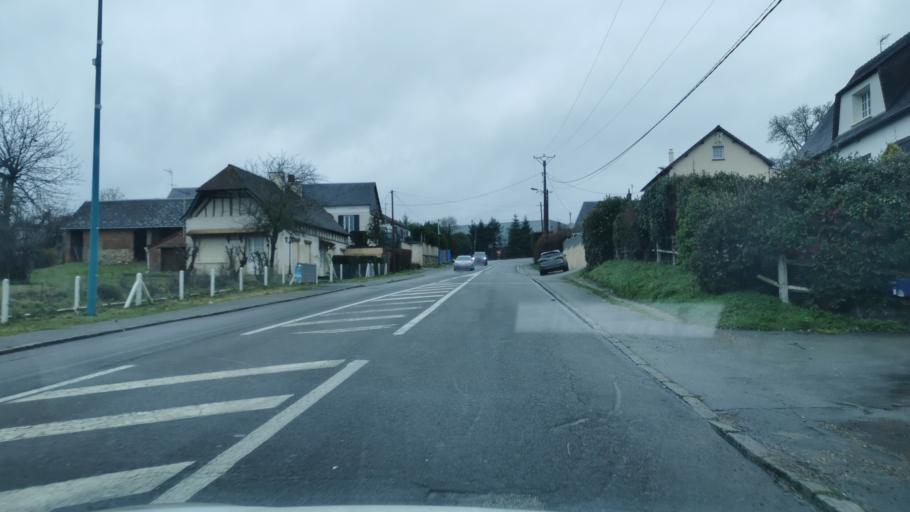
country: FR
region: Haute-Normandie
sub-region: Departement de l'Eure
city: Gravigny
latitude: 49.0670
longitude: 1.1728
